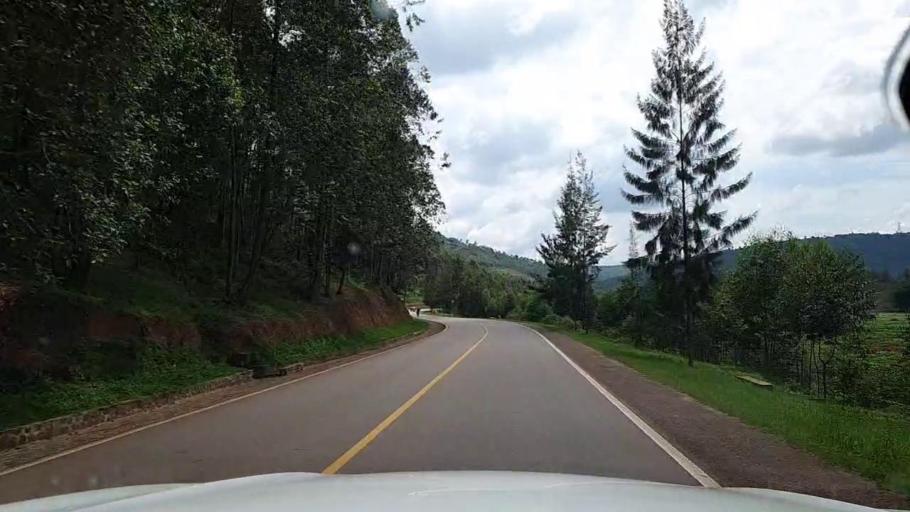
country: RW
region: Kigali
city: Kigali
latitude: -1.8122
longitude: 30.1019
